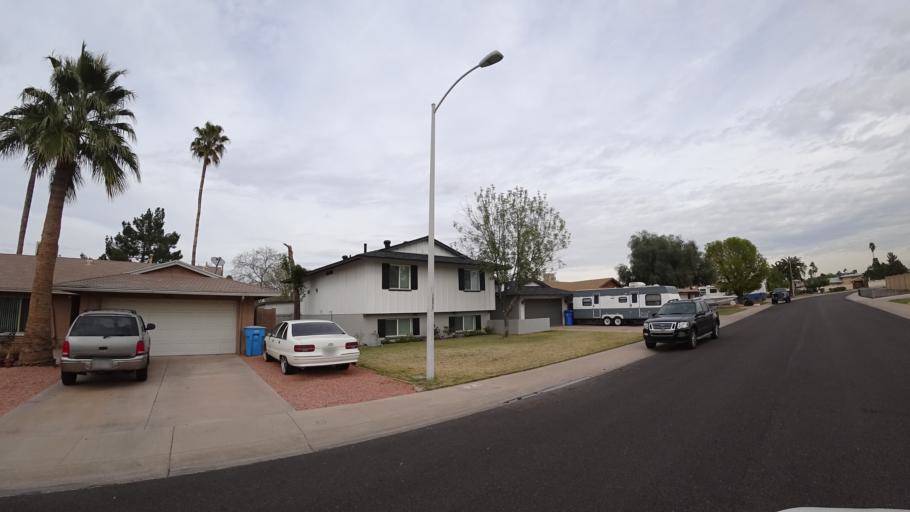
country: US
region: Arizona
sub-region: Maricopa County
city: Glendale
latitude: 33.6144
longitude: -112.1320
